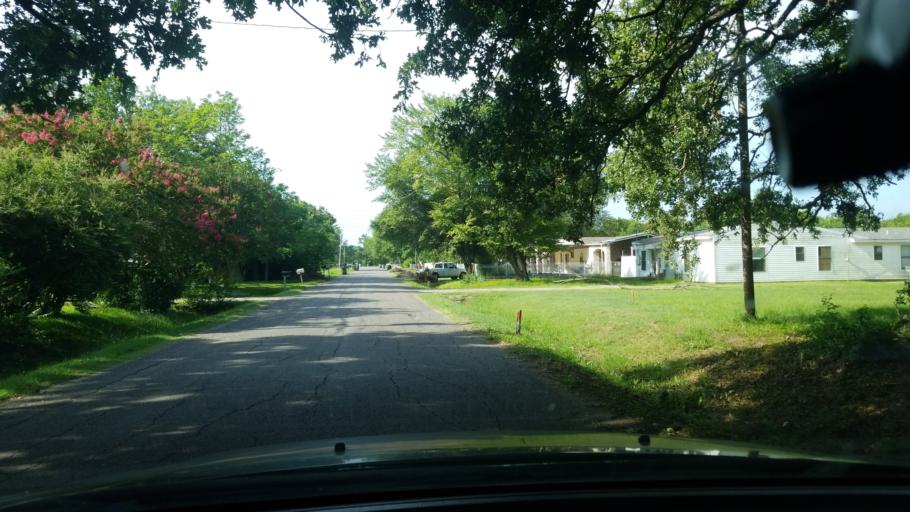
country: US
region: Texas
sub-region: Dallas County
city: Balch Springs
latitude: 32.7146
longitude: -96.6364
